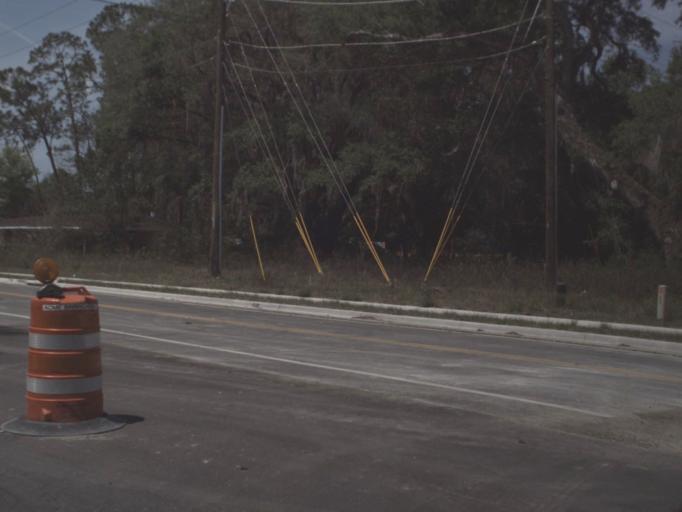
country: US
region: Florida
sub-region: Sumter County
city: Bushnell
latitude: 28.6686
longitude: -82.1228
